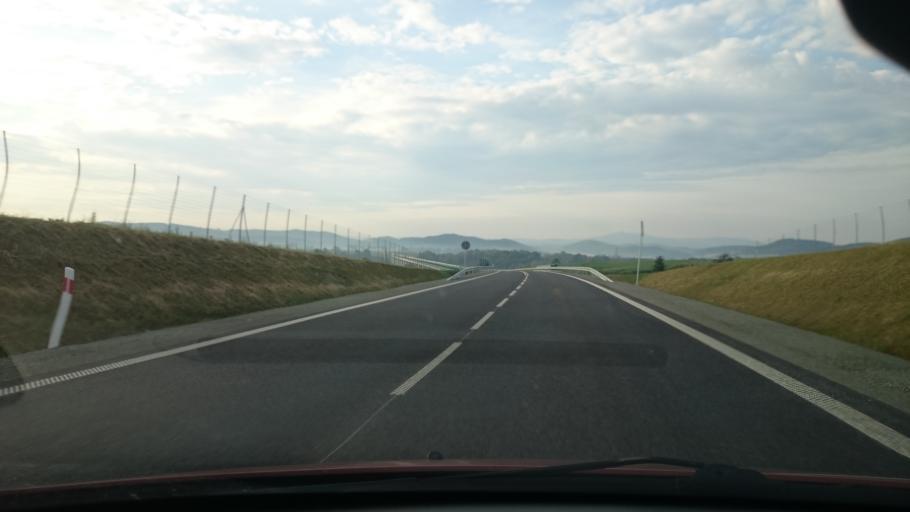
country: PL
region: Lower Silesian Voivodeship
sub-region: Powiat klodzki
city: Klodzko
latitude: 50.4094
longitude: 16.6305
